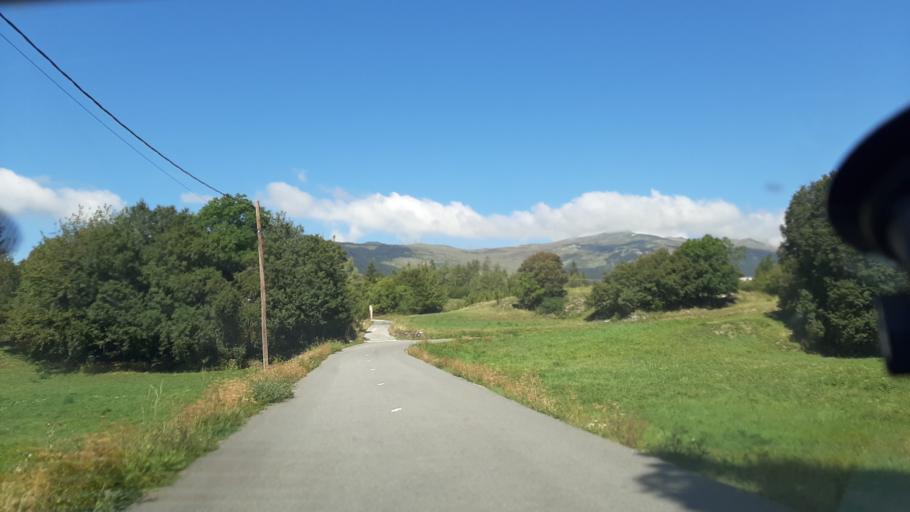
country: FR
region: Rhone-Alpes
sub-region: Departement de la Savoie
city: Aime
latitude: 45.5142
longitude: 6.5960
